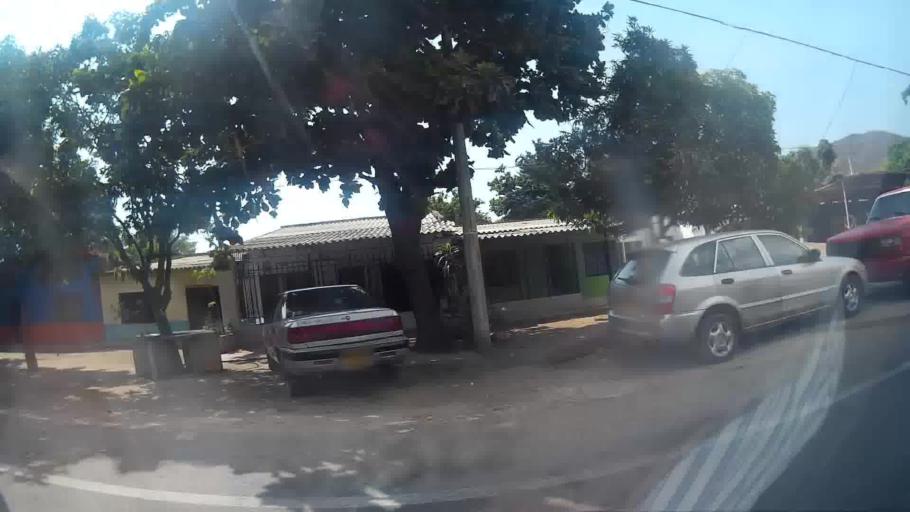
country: CO
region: Magdalena
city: Santa Marta
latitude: 11.1879
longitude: -74.2171
